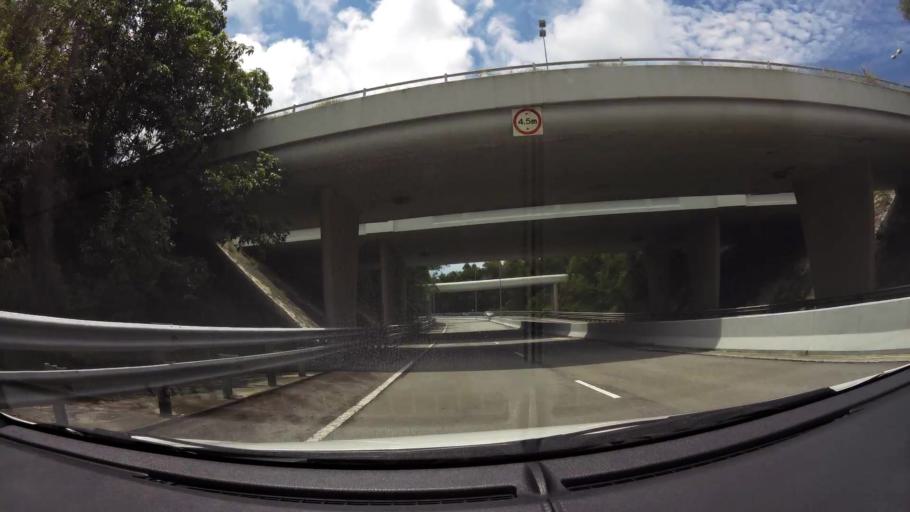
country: BN
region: Brunei and Muara
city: Bandar Seri Begawan
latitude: 4.9742
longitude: 114.8808
